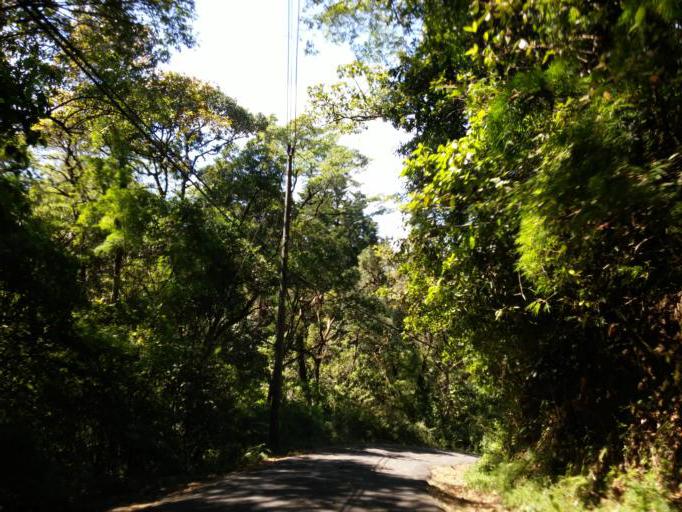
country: CR
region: Heredia
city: Santo Domingo
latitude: 10.0971
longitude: -84.1174
